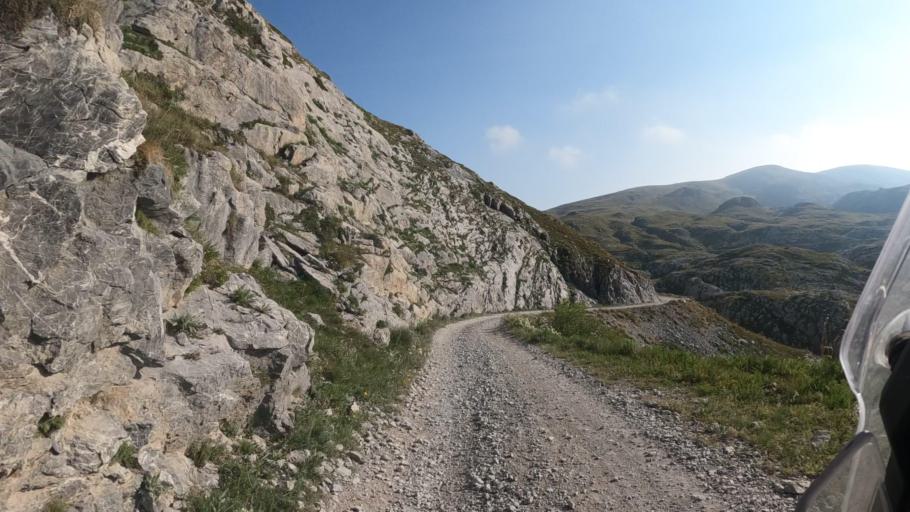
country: IT
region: Piedmont
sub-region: Provincia di Cuneo
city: Limone Piemonte
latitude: 44.1717
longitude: 7.6356
